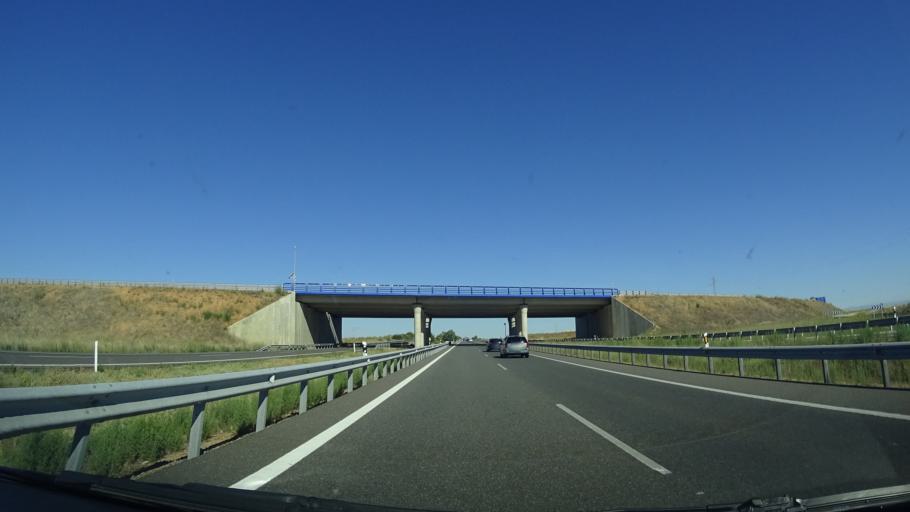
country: ES
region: Castille and Leon
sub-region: Provincia de Zamora
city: Castrogonzalo
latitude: 41.9660
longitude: -5.5913
